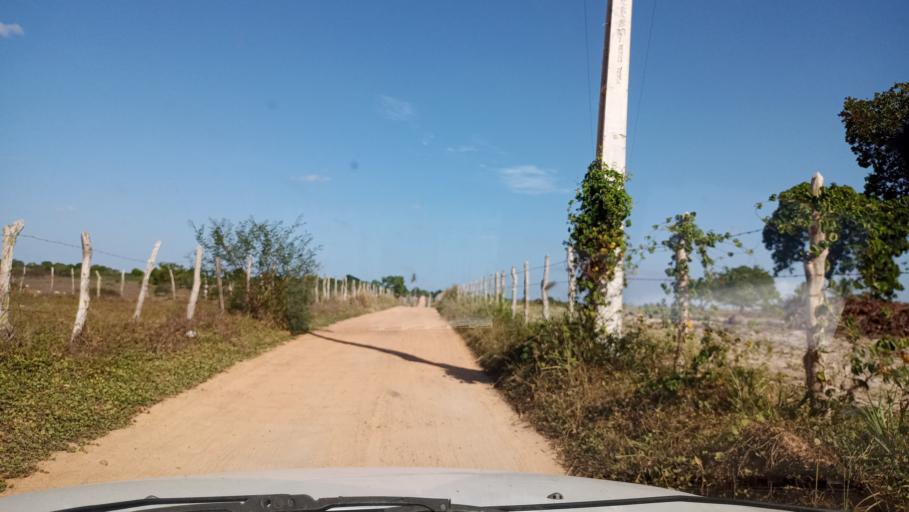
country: BR
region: Rio Grande do Norte
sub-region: Brejinho
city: Brejinho
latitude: -6.1758
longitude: -35.4629
